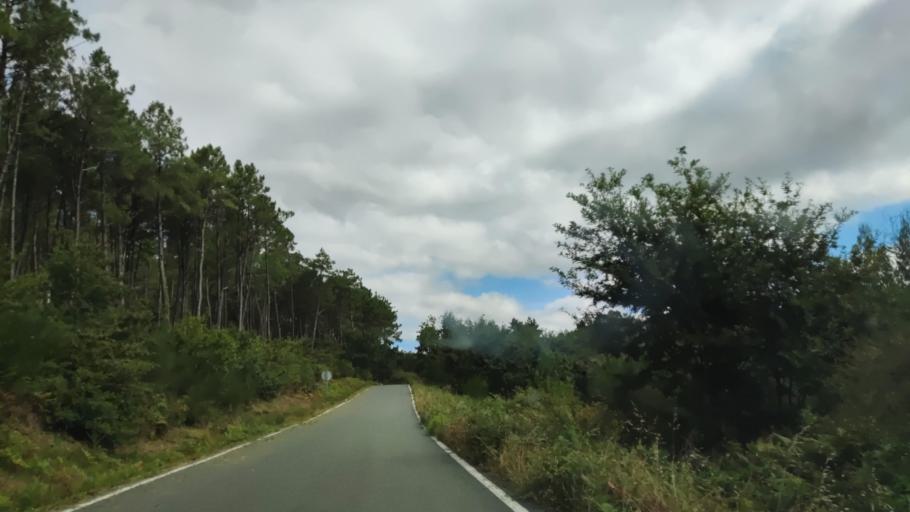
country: ES
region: Galicia
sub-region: Provincia da Coruna
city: Rois
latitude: 42.7314
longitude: -8.7068
